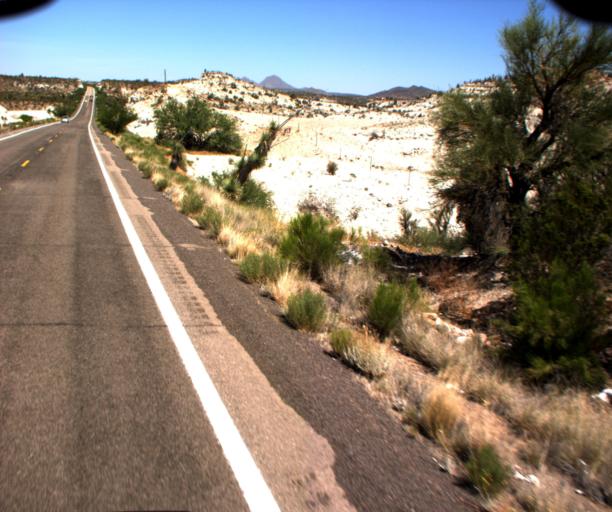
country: US
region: Arizona
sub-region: Graham County
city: Bylas
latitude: 33.2478
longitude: -110.2712
